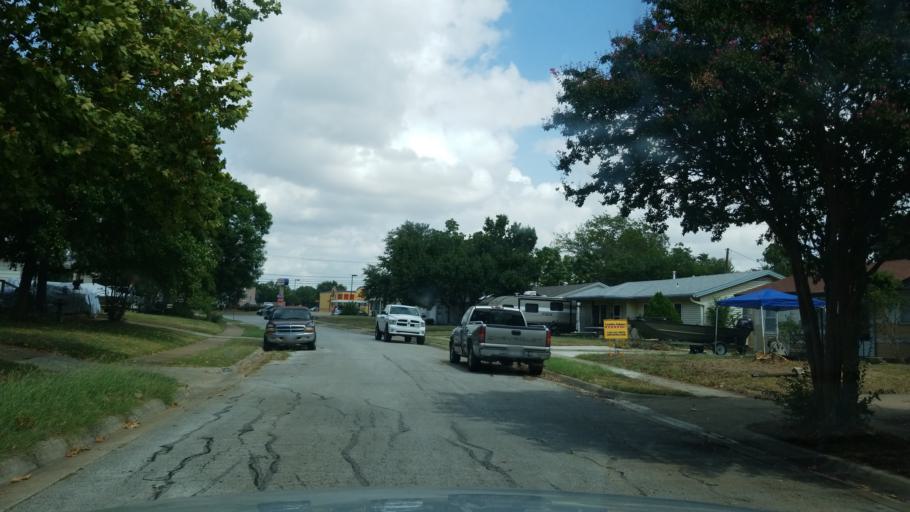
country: US
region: Texas
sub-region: Tarrant County
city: Euless
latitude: 32.8508
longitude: -97.0859
